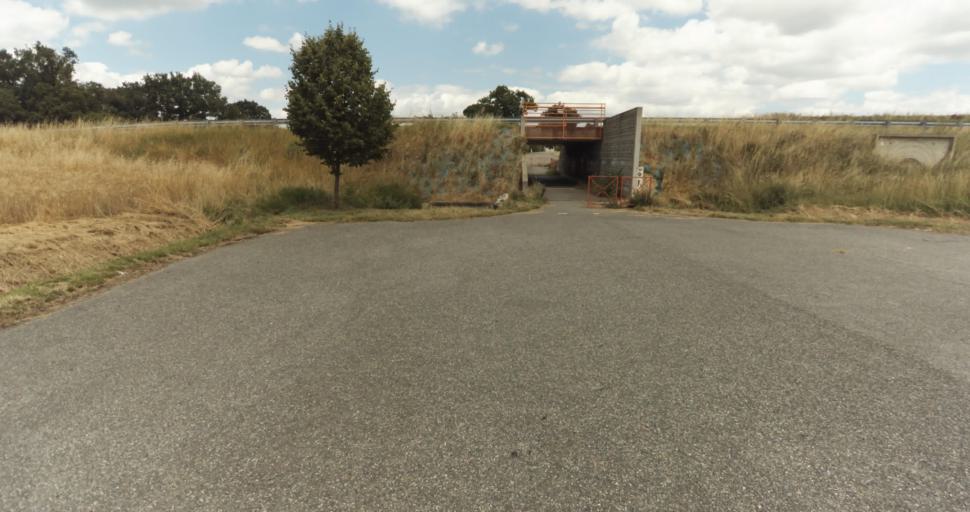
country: FR
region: Midi-Pyrenees
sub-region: Departement de la Haute-Garonne
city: Fontenilles
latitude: 43.5473
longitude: 1.1867
